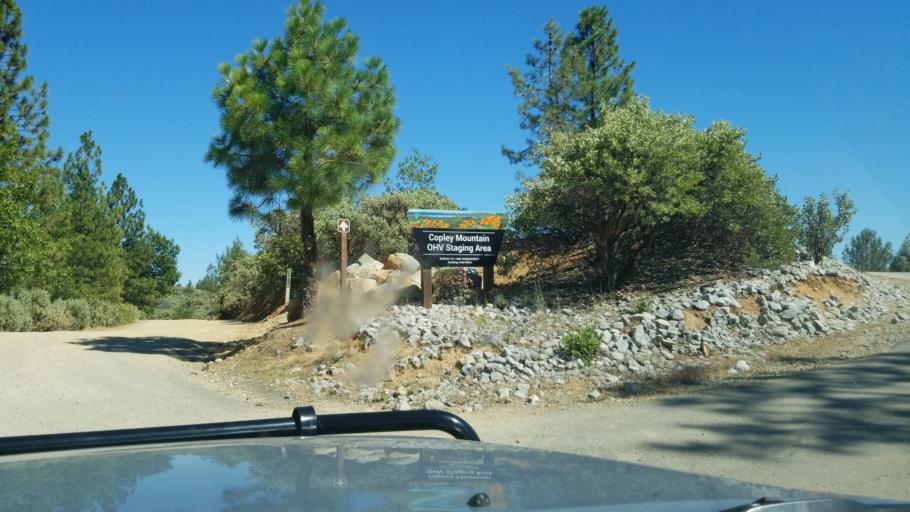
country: US
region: California
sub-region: Shasta County
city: Shasta
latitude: 40.6599
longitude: -122.4669
